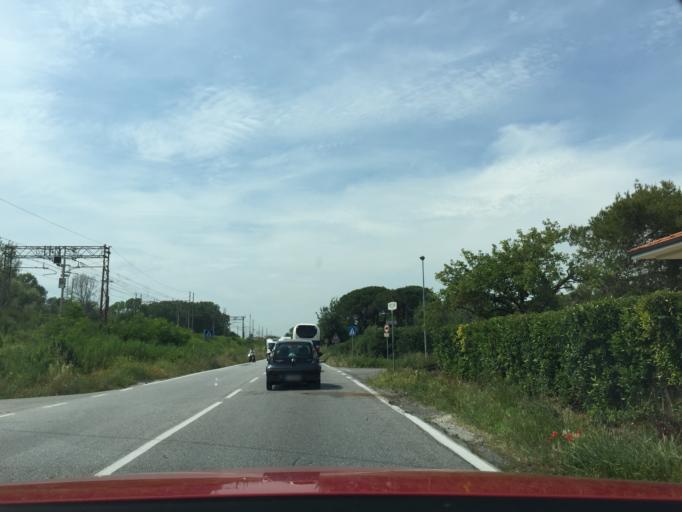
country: IT
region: Tuscany
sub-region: Province of Pisa
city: Migliarino
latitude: 43.7590
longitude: 10.3501
